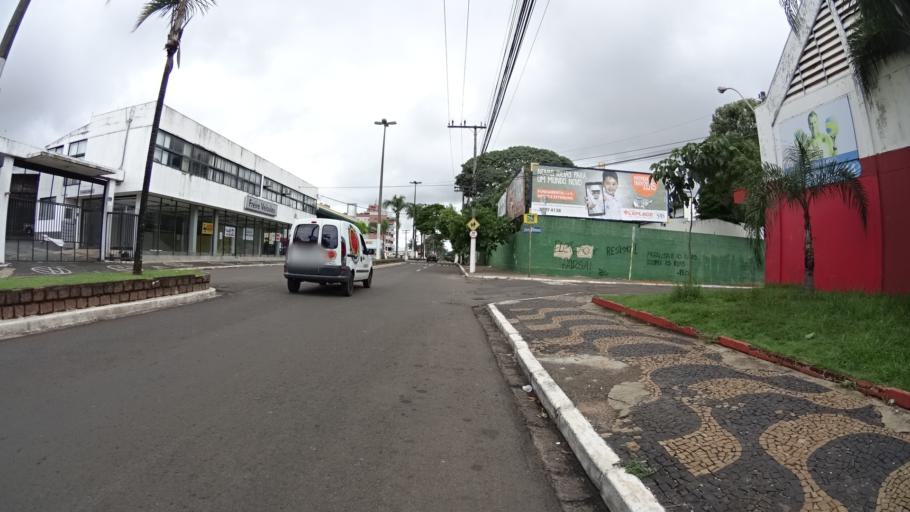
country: BR
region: Sao Paulo
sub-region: Marilia
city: Marilia
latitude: -22.2233
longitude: -49.9567
